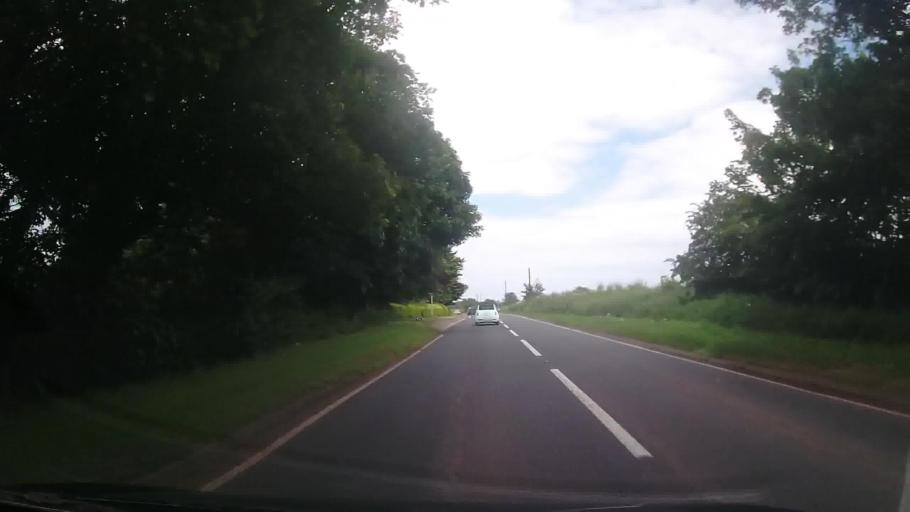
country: GB
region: England
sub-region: Herefordshire
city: Belmont
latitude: 52.0284
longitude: -2.7735
